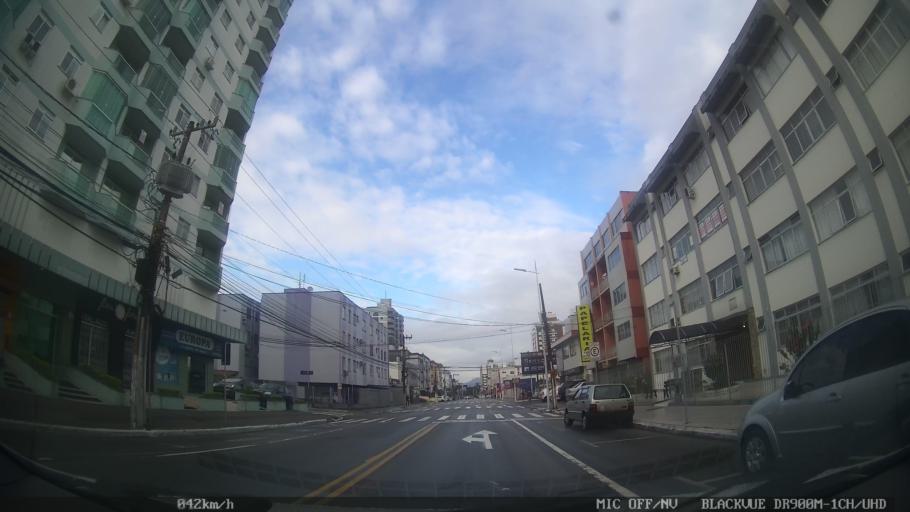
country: BR
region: Santa Catarina
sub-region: Sao Jose
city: Campinas
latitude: -27.5936
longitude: -48.6135
